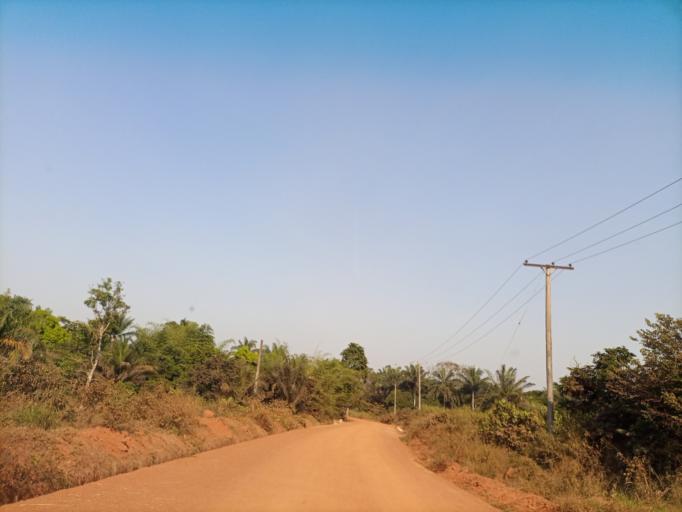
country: NG
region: Enugu
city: Opi
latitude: 6.7760
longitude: 7.3845
